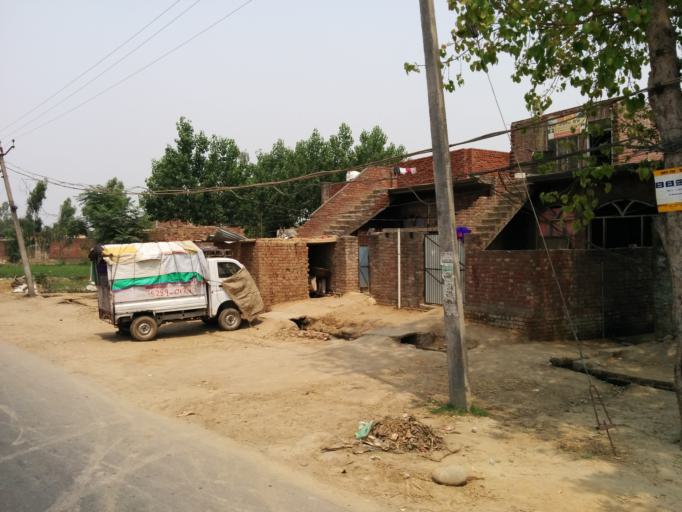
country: IN
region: Punjab
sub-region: Gurdaspur
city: Dhariwal
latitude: 31.9310
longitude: 75.3046
